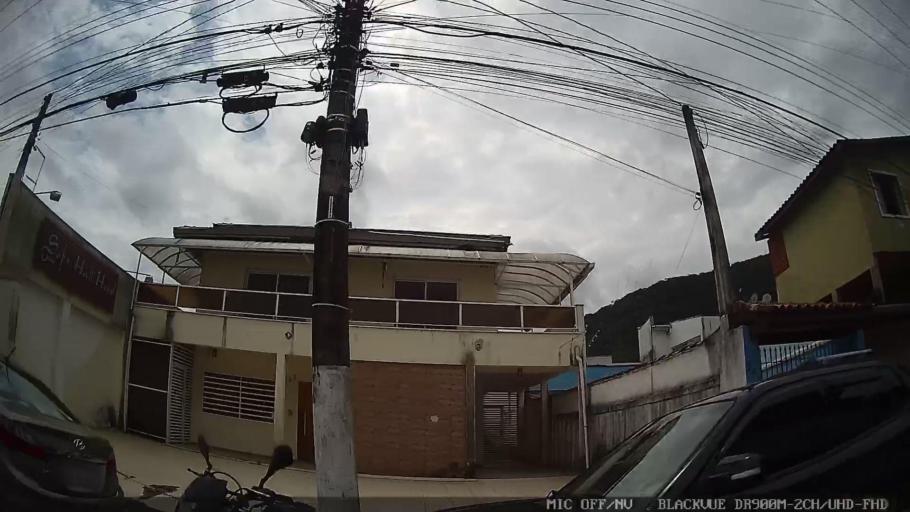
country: BR
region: Sao Paulo
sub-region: Caraguatatuba
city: Caraguatatuba
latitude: -23.6199
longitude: -45.4075
